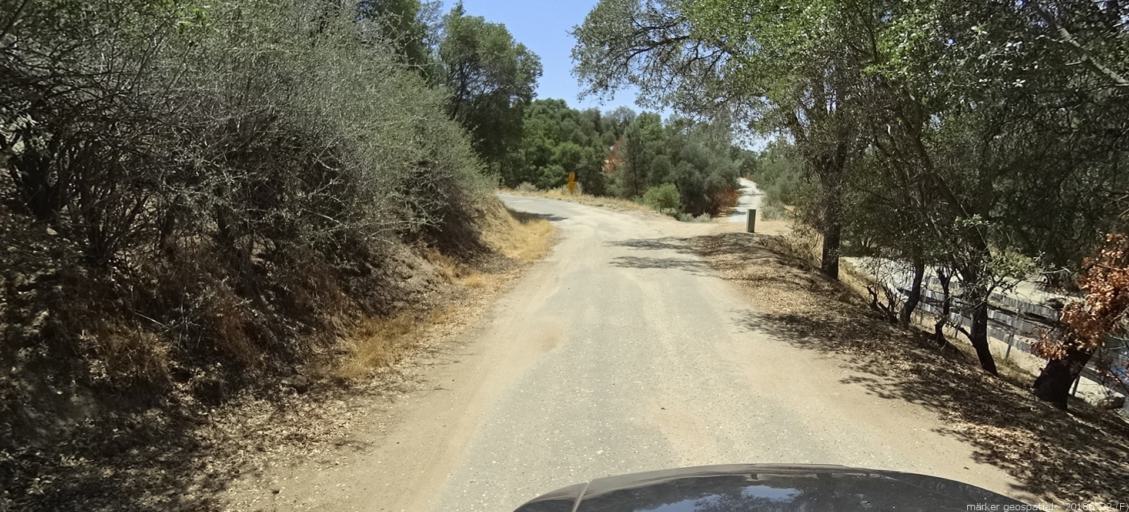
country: US
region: California
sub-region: Madera County
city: Coarsegold
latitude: 37.2410
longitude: -119.7348
